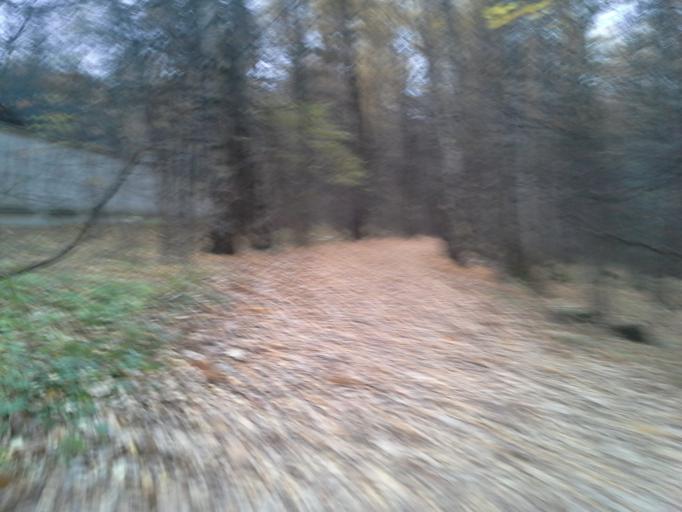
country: RU
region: Moscow
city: Zyuzino
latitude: 55.6220
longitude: 37.5760
